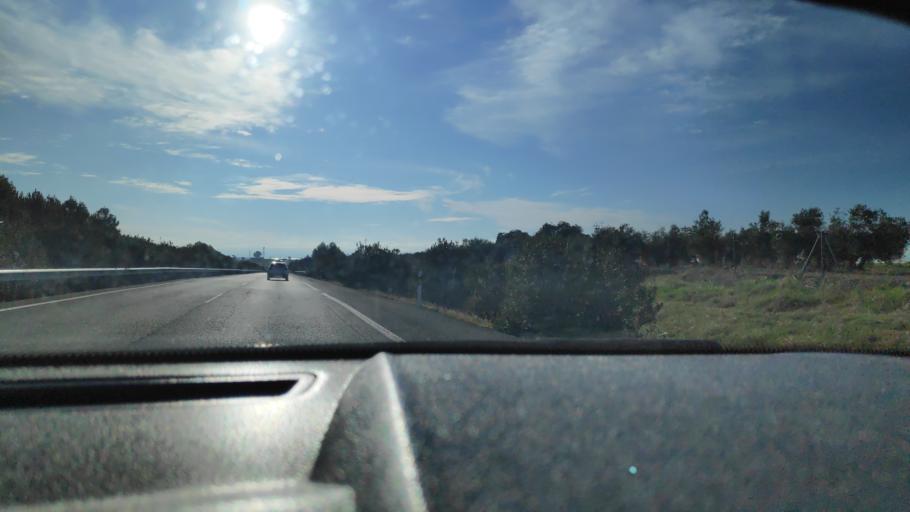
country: ES
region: Andalusia
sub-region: Province of Cordoba
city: La Carlota
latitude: 37.7085
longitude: -4.9091
